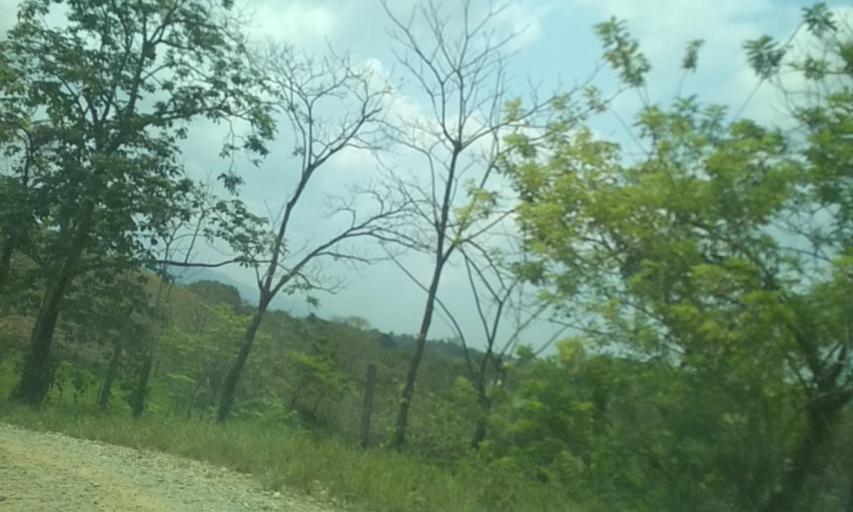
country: MX
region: Tabasco
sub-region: Huimanguillo
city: Francisco Rueda
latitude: 17.6107
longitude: -93.8098
